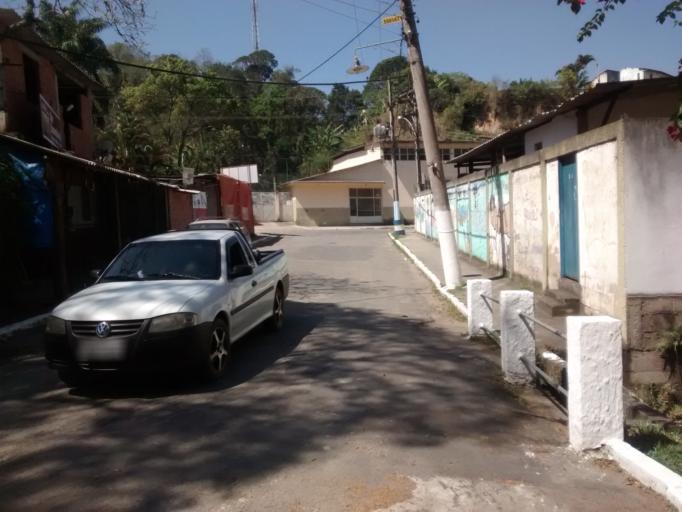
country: BR
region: Rio de Janeiro
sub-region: Vassouras
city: Vassouras
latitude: -22.4752
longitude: -43.5829
